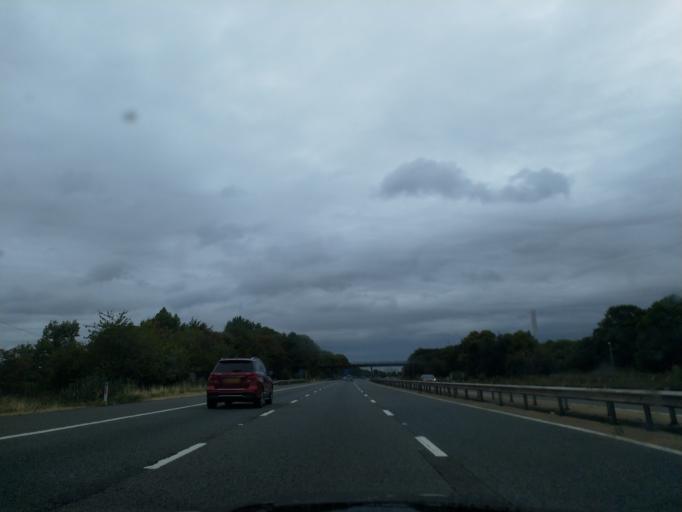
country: GB
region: England
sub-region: Surrey
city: Shepperton
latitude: 51.4061
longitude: -0.4446
